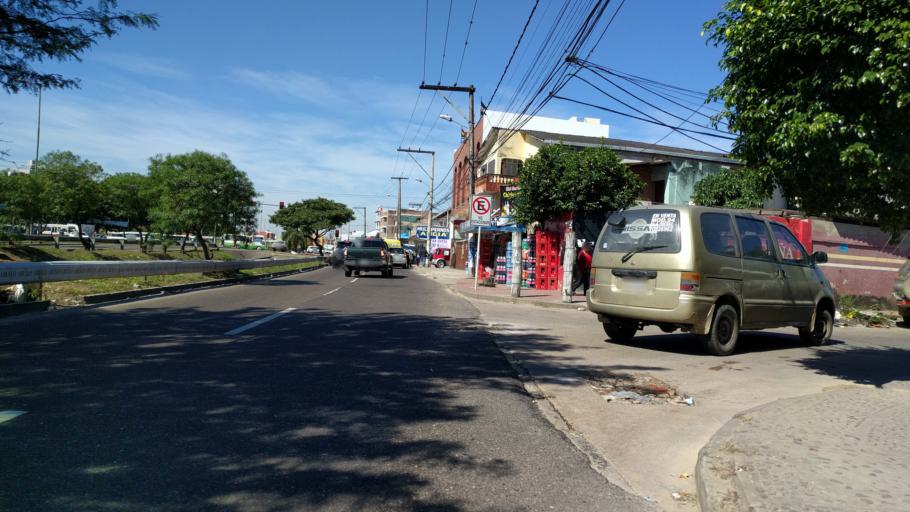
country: BO
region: Santa Cruz
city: Santa Cruz de la Sierra
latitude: -17.7972
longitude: -63.1936
